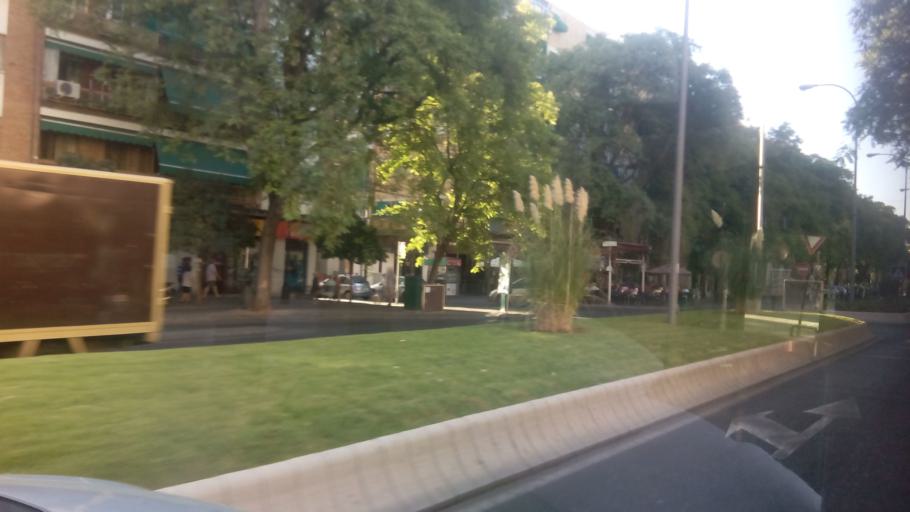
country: ES
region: Andalusia
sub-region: Province of Cordoba
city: Cordoba
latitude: 37.8889
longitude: -4.7643
